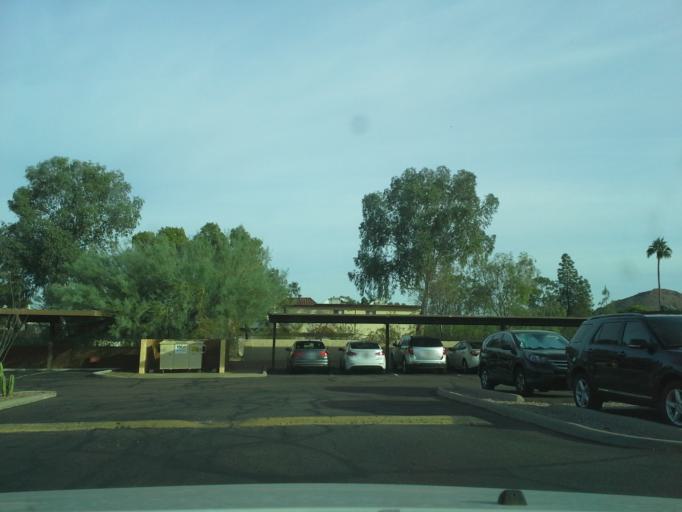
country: US
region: Arizona
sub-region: Maricopa County
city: Glendale
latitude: 33.6083
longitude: -112.0639
